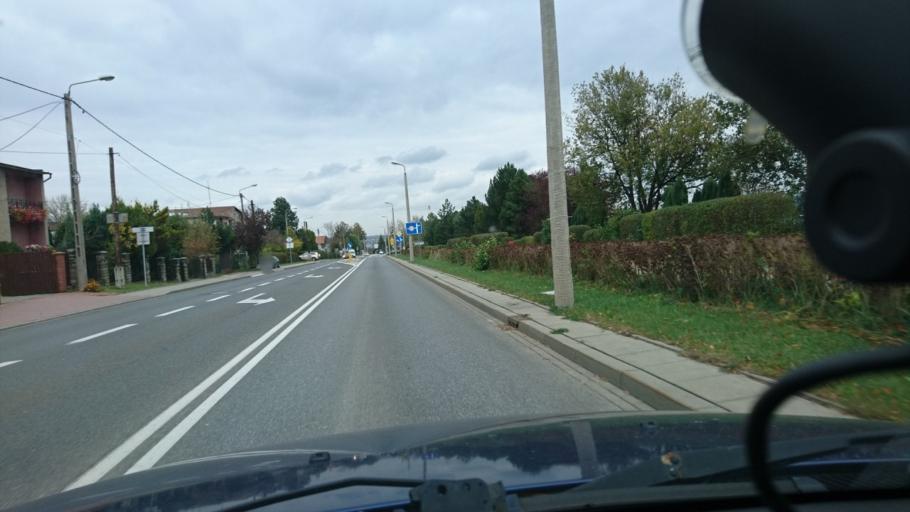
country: PL
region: Silesian Voivodeship
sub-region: Bielsko-Biala
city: Bielsko-Biala
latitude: 49.7926
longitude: 19.0371
